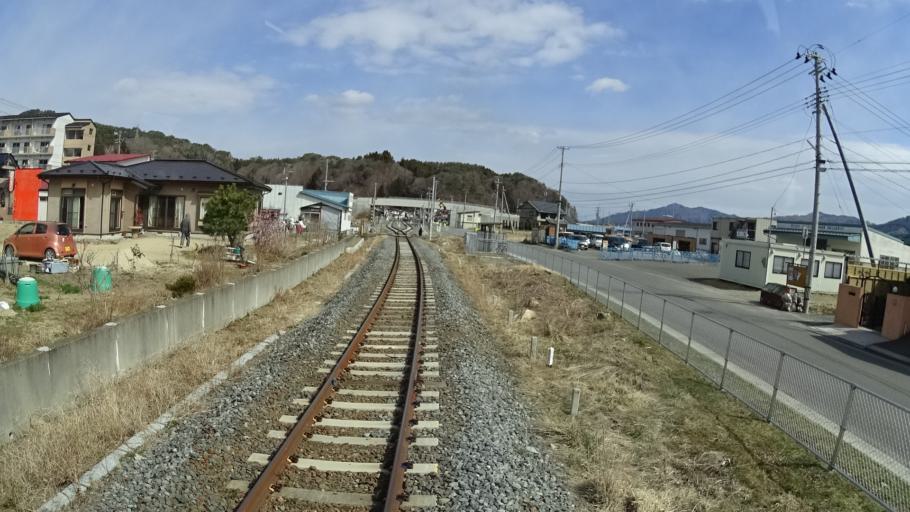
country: JP
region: Iwate
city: Miyako
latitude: 39.5794
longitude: 141.9366
